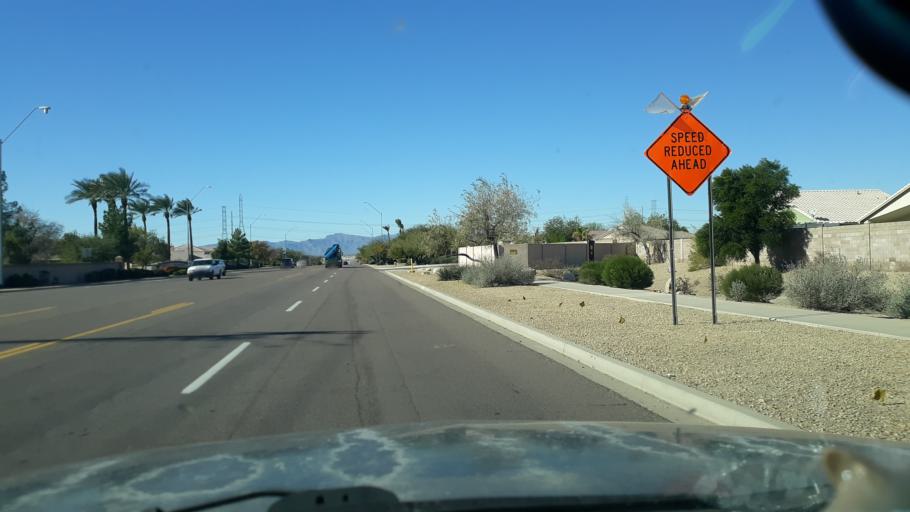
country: US
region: Arizona
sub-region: Maricopa County
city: Youngtown
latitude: 33.5512
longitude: -112.2931
